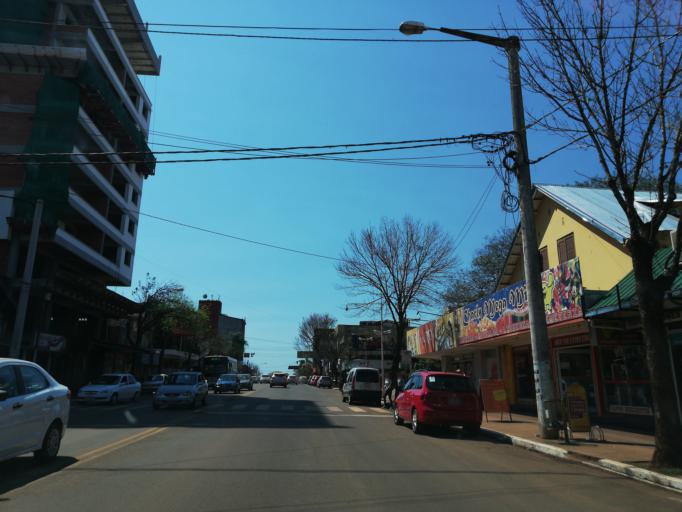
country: AR
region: Misiones
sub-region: Departamento de Eldorado
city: Eldorado
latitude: -26.4084
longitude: -54.6076
